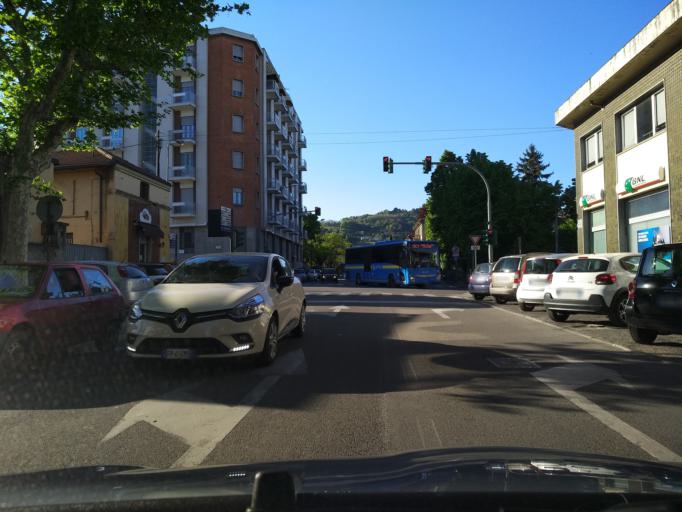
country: IT
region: Piedmont
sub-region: Provincia di Torino
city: Pinerolo
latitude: 44.8857
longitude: 7.3379
